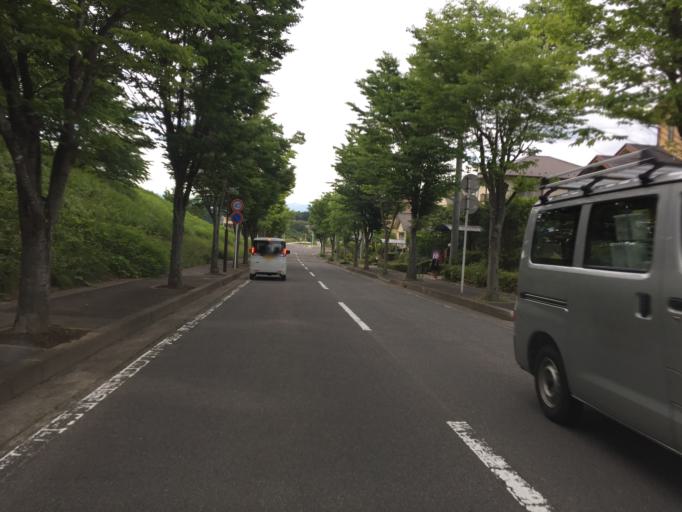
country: JP
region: Fukushima
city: Fukushima-shi
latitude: 37.6640
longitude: 140.4706
